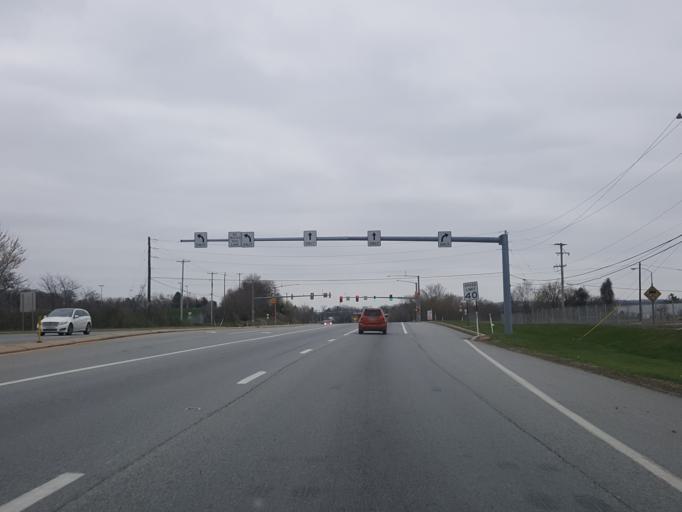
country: US
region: Pennsylvania
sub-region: York County
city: North York
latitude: 39.9833
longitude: -76.7173
